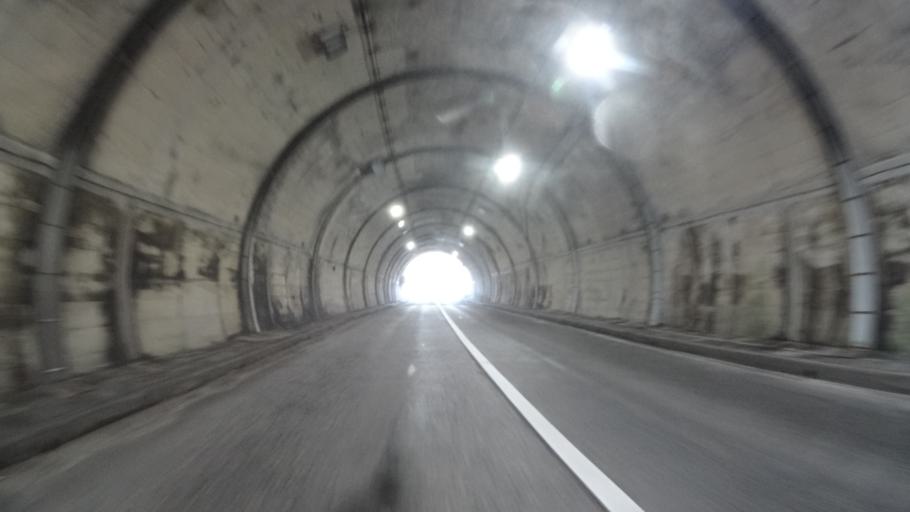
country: JP
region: Ishikawa
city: Hakui
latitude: 37.1233
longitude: 136.7277
